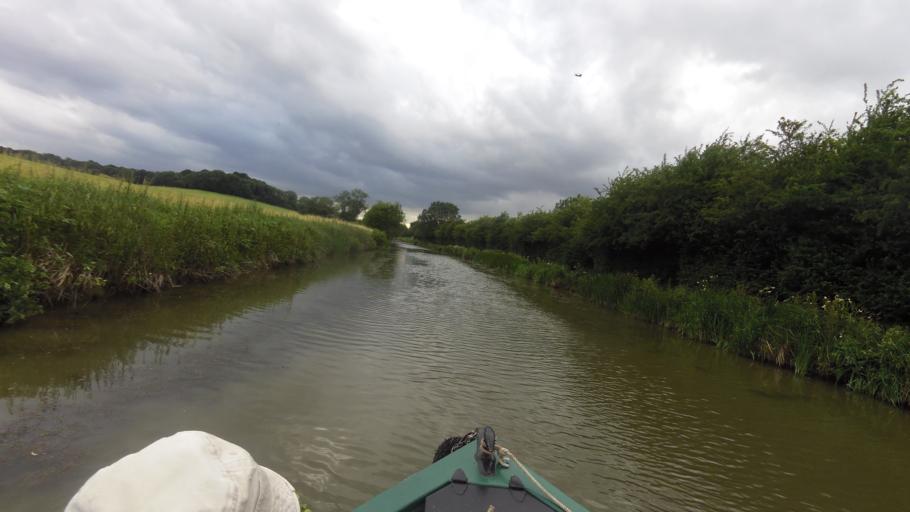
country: GB
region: England
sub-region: West Berkshire
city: Kintbury
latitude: 51.4022
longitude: -1.4069
